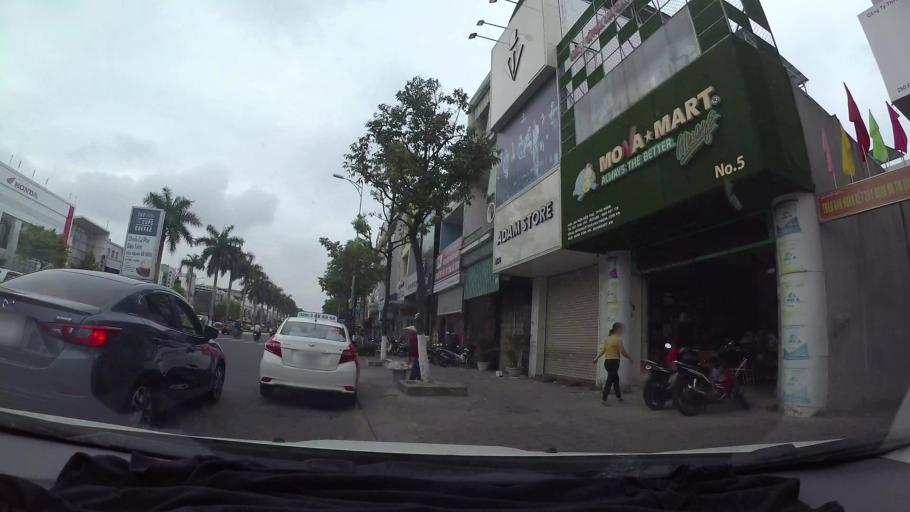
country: VN
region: Da Nang
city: Thanh Khe
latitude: 16.0659
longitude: 108.1950
